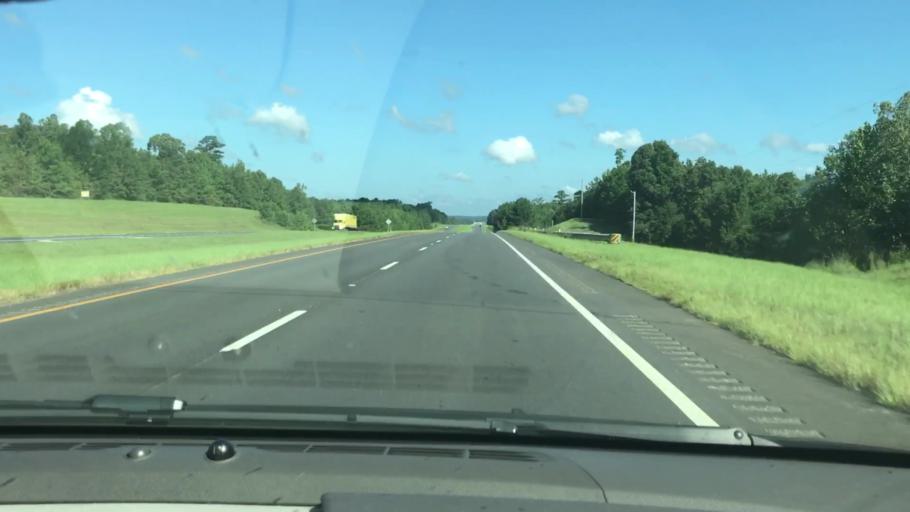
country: US
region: Alabama
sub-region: Barbour County
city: Eufaula
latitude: 32.0387
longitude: -85.1265
